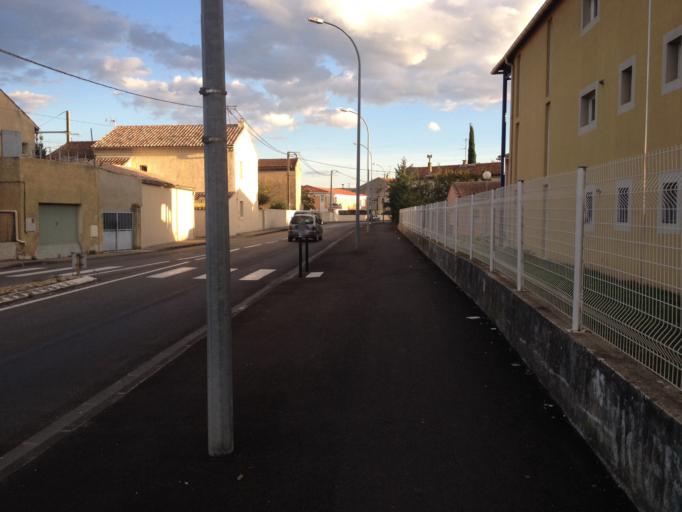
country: FR
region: Provence-Alpes-Cote d'Azur
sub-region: Departement du Vaucluse
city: Orange
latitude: 44.1414
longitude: 4.8135
